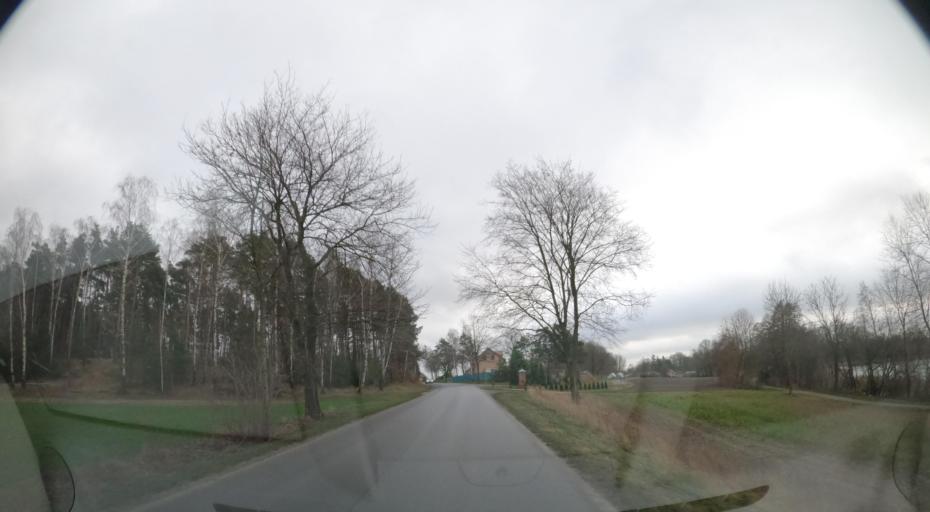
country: PL
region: Greater Poland Voivodeship
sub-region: Powiat pilski
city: Lobzenica
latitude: 53.2482
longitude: 17.2834
